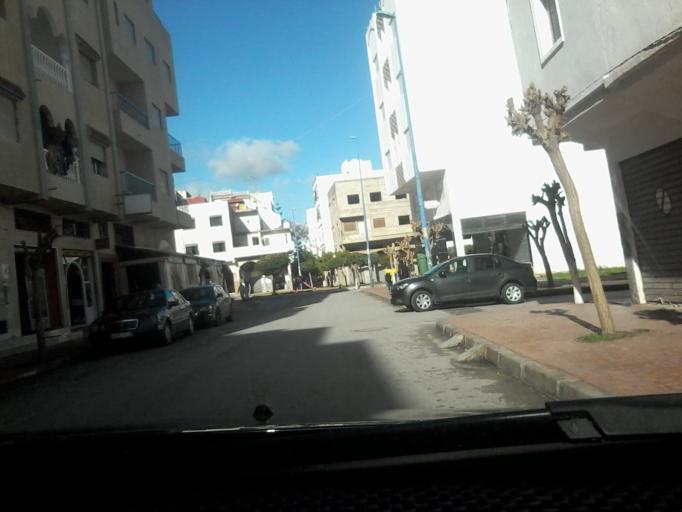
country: MA
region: Tanger-Tetouan
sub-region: Tetouan
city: Martil
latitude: 35.6849
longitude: -5.3269
